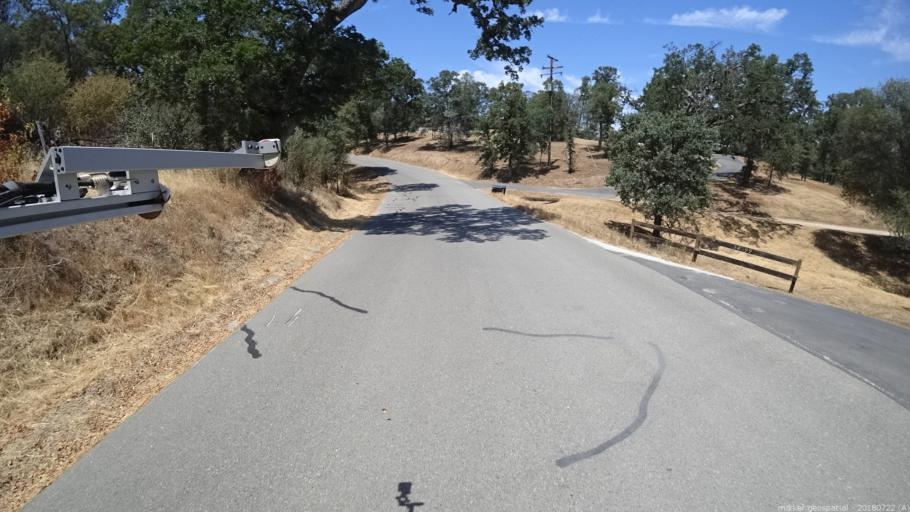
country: US
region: California
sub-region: Madera County
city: Coarsegold
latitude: 37.2443
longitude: -119.7250
